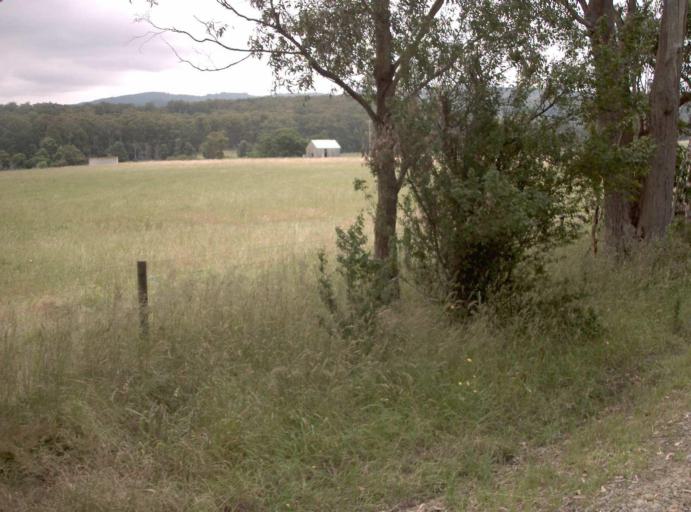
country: AU
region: Victoria
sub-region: Latrobe
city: Traralgon
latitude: -38.4866
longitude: 146.6807
